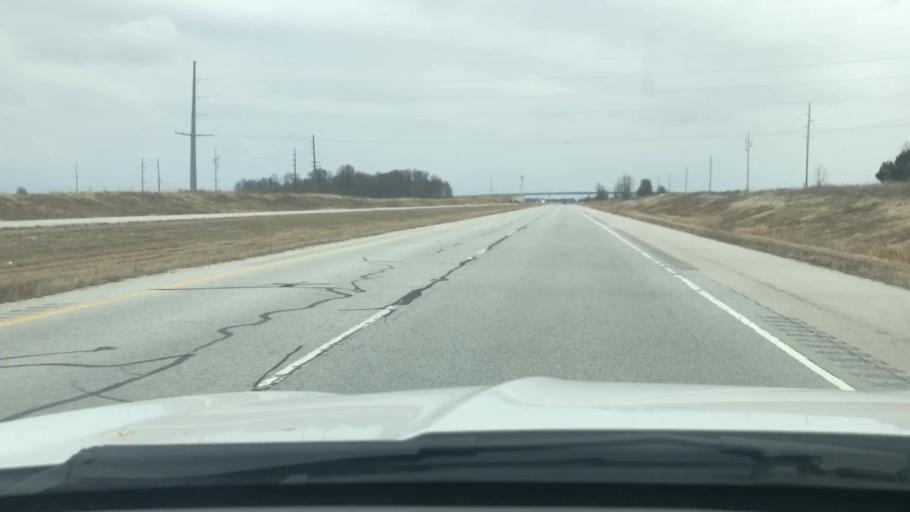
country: US
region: Indiana
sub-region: Cass County
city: Georgetown
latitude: 40.6567
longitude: -86.5460
